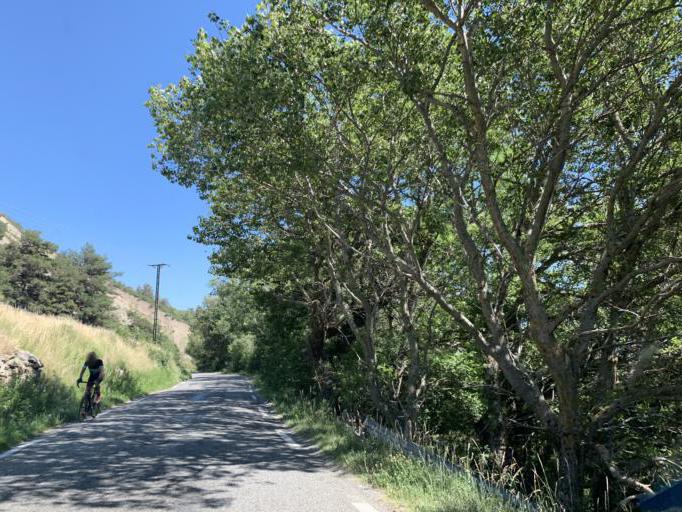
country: FR
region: Provence-Alpes-Cote d'Azur
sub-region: Departement des Hautes-Alpes
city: La Batie-Neuve
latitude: 44.5972
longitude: 6.1483
